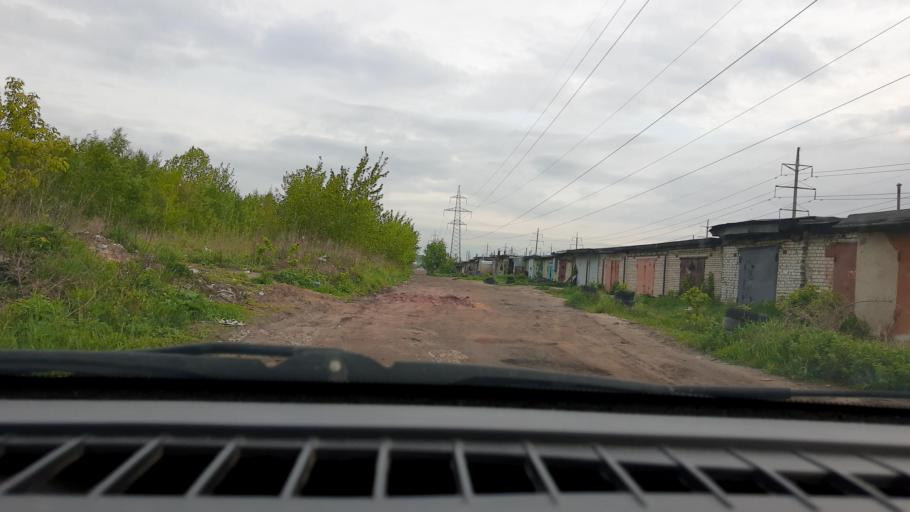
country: RU
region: Nizjnij Novgorod
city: Nizhniy Novgorod
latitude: 56.2720
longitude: 43.8979
